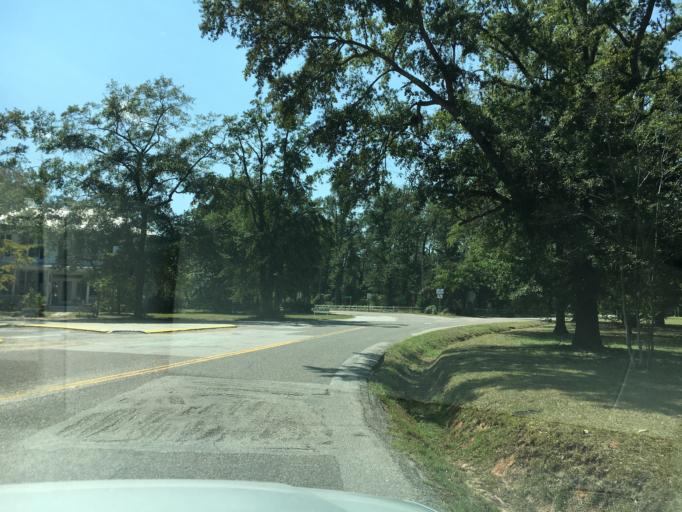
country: US
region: South Carolina
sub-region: Lexington County
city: Batesburg
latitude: 33.8433
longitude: -81.6621
